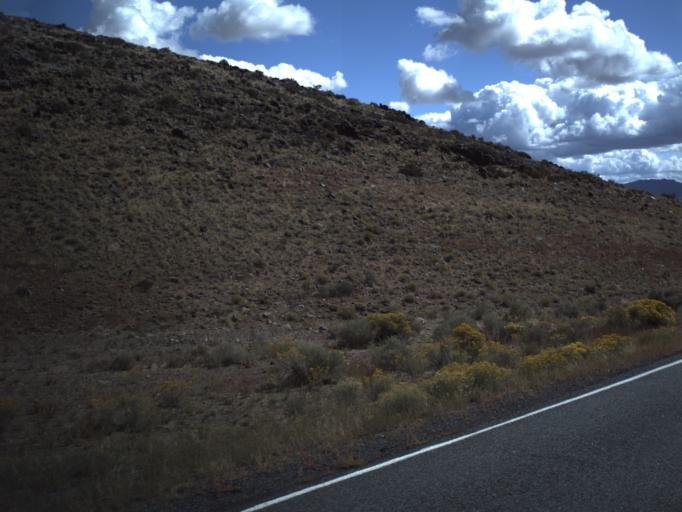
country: US
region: Utah
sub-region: Beaver County
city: Milford
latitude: 38.6137
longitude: -113.8394
